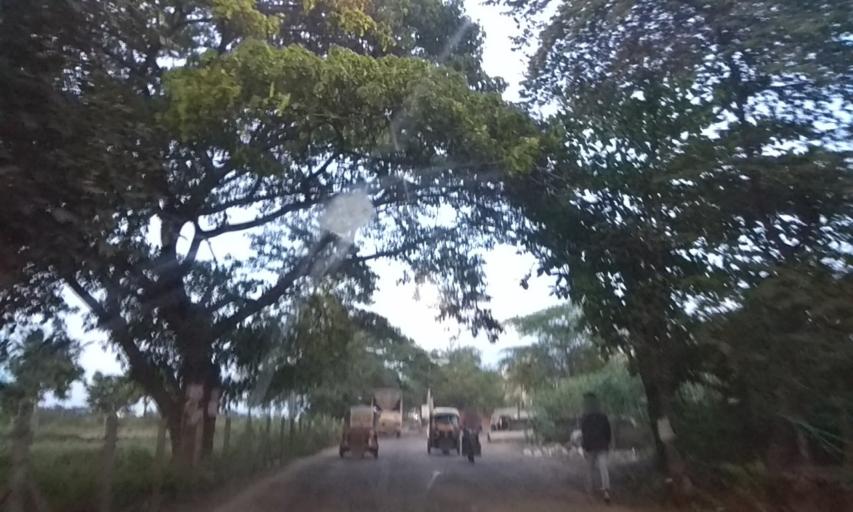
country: IN
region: Maharashtra
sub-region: Pune Division
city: Pune
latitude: 18.5199
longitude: 73.9184
